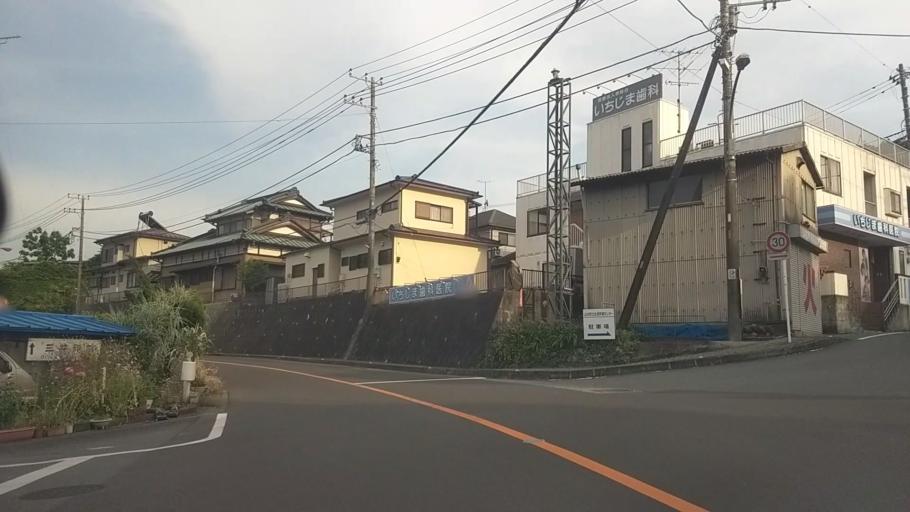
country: JP
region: Kanagawa
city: Odawara
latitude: 35.3610
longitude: 139.0844
